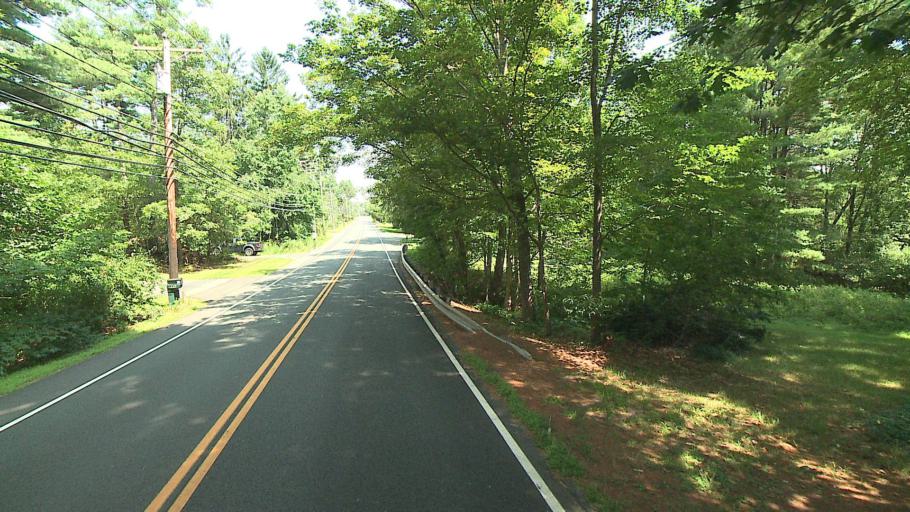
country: US
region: Connecticut
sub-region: Hartford County
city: Collinsville
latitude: 41.7691
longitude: -72.8908
